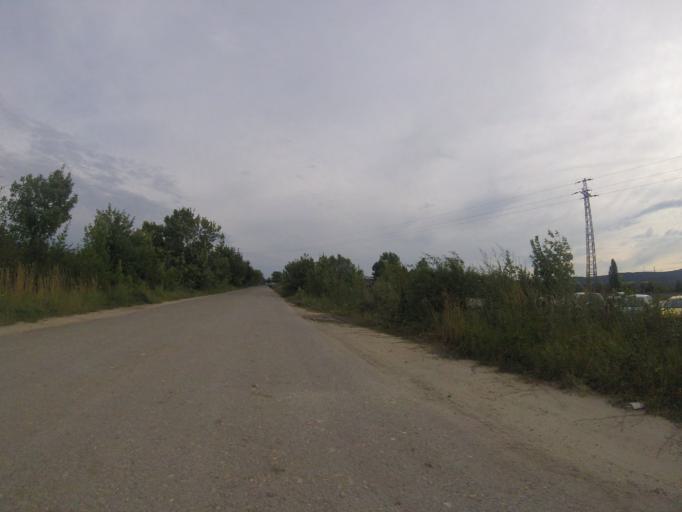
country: HU
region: Pest
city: Budakalasz
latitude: 47.6228
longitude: 19.0695
